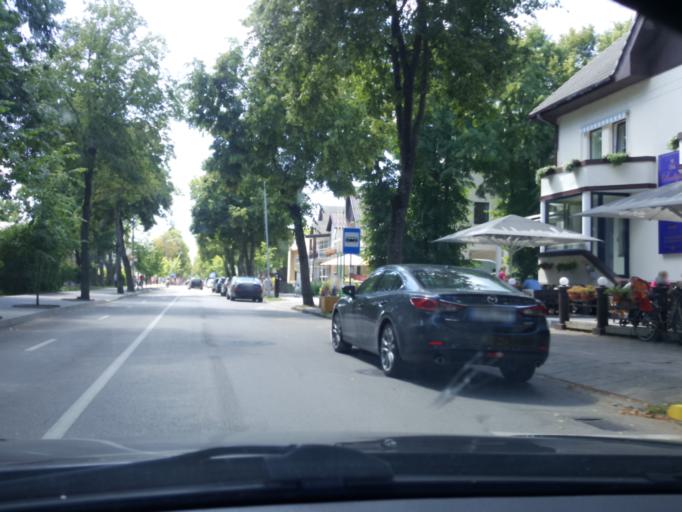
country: LT
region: Klaipedos apskritis
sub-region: Klaipeda
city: Palanga
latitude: 55.9246
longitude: 21.0706
